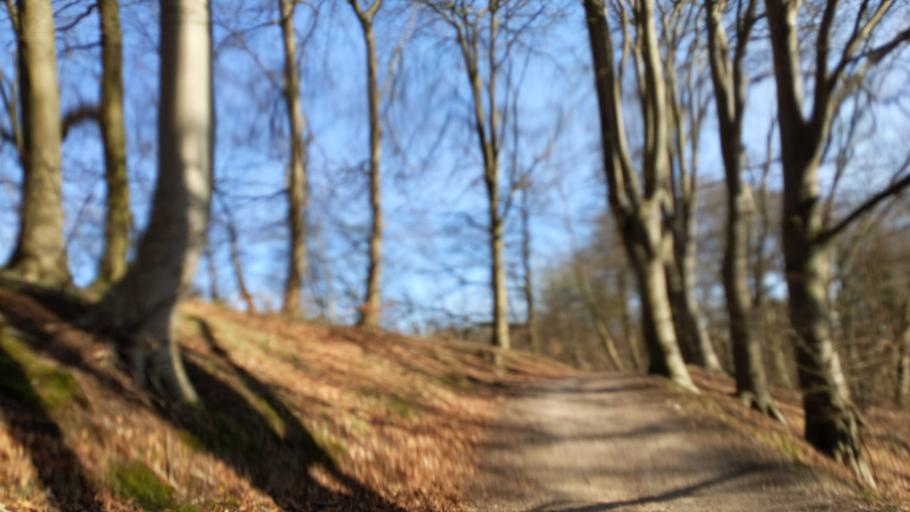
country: DE
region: Schleswig-Holstein
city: Timmendorfer Strand
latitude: 53.9846
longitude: 10.8247
